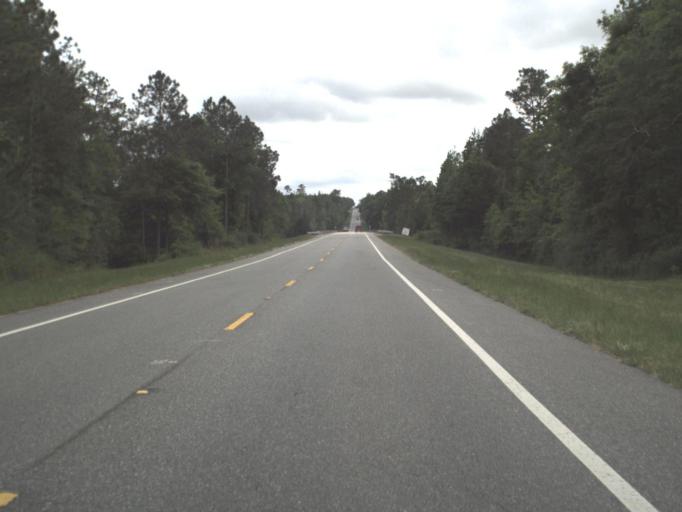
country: US
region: Florida
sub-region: Santa Rosa County
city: Point Baker
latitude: 30.7923
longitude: -87.0414
